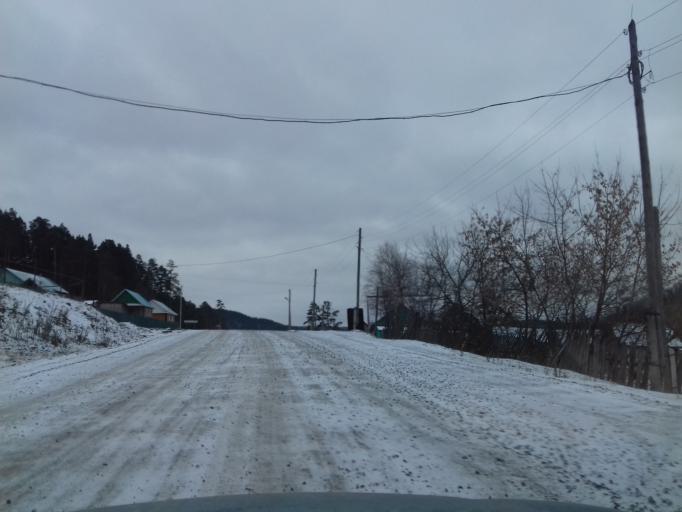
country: RU
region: Bashkortostan
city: Starosubkhangulovo
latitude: 53.0914
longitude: 57.4268
